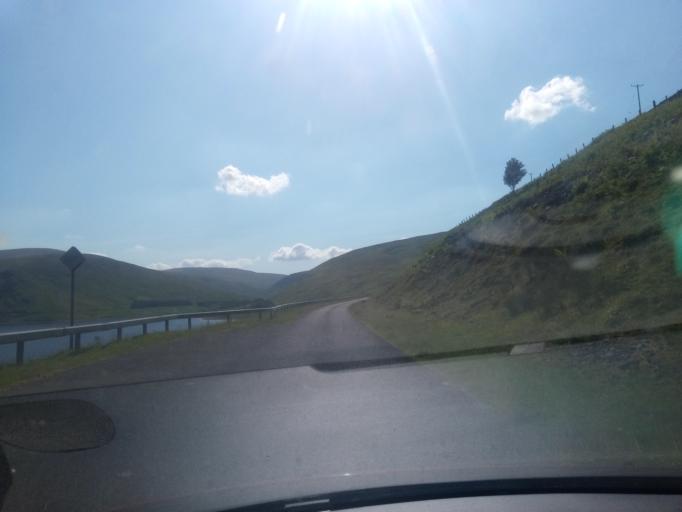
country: GB
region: Scotland
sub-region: The Scottish Borders
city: Peebles
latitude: 55.4881
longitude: -3.2877
